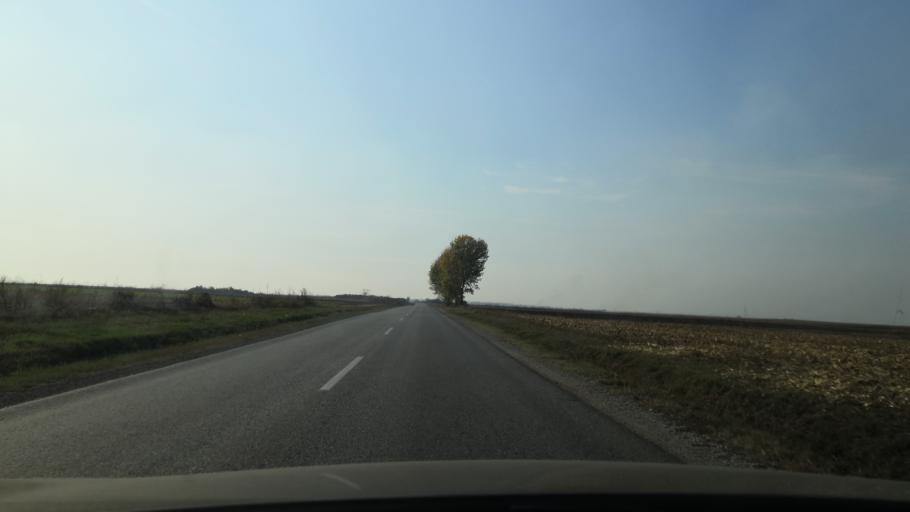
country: RS
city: Ljukovo
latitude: 44.9883
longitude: 20.0228
